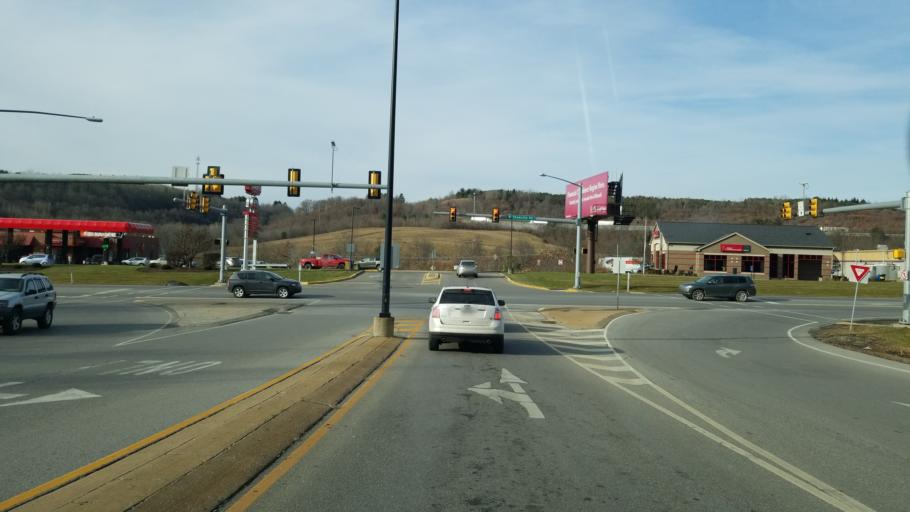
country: US
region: Pennsylvania
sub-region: Clearfield County
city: Clearfield
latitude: 41.0338
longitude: -78.4031
